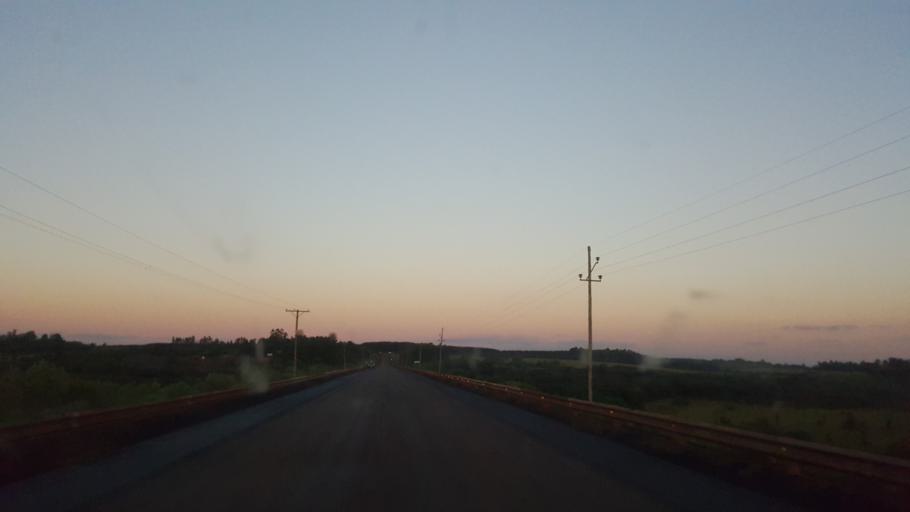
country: AR
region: Corrientes
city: Garruchos
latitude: -28.2336
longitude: -55.8147
